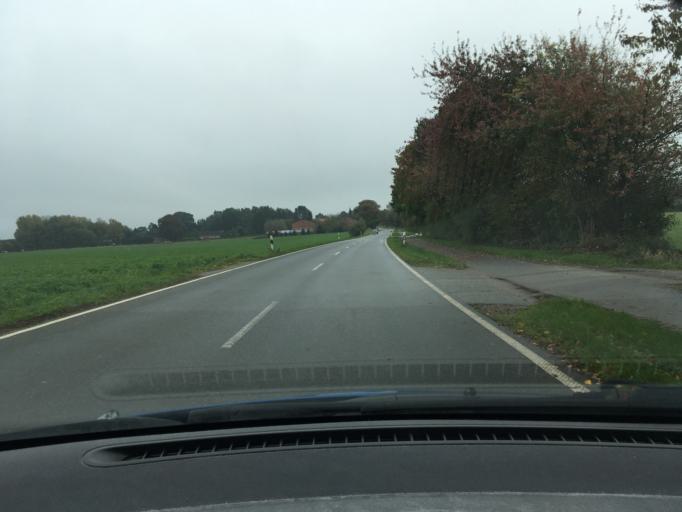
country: DE
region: Schleswig-Holstein
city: Bosdorf
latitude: 54.1144
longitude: 10.4774
